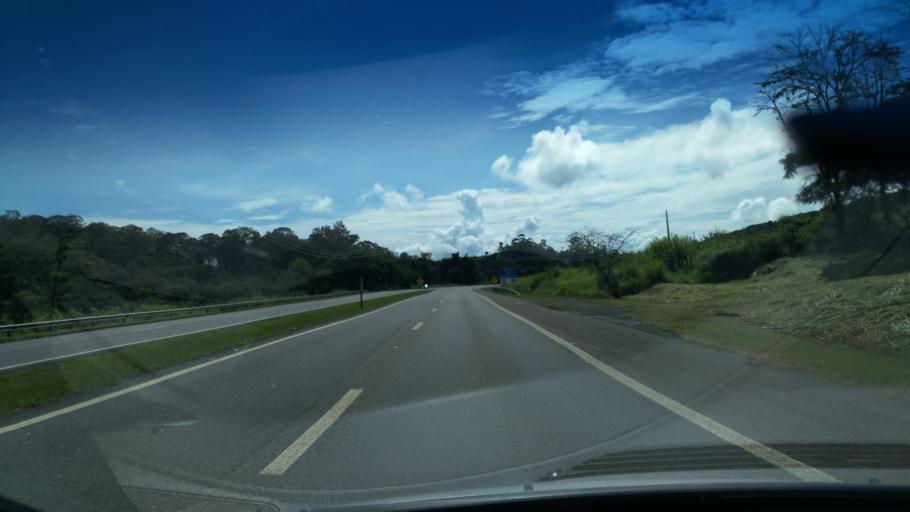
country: BR
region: Sao Paulo
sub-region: Santo Antonio Do Jardim
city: Espirito Santo do Pinhal
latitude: -22.2261
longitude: -46.7939
